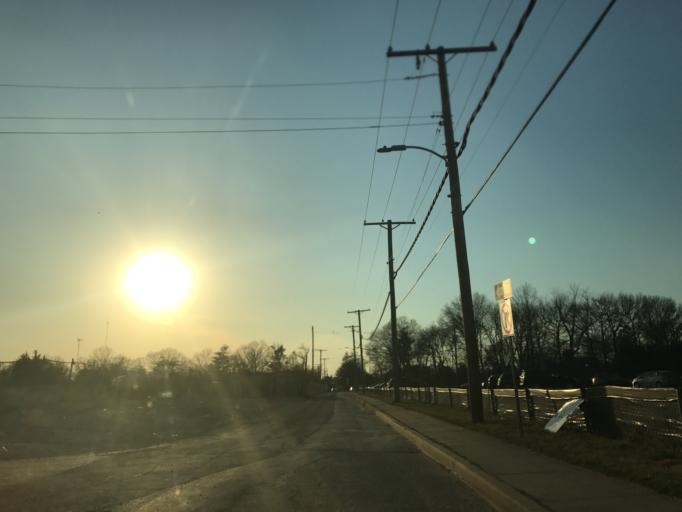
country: US
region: Maryland
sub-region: City of Baltimore
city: Baltimore
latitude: 39.3452
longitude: -76.6145
